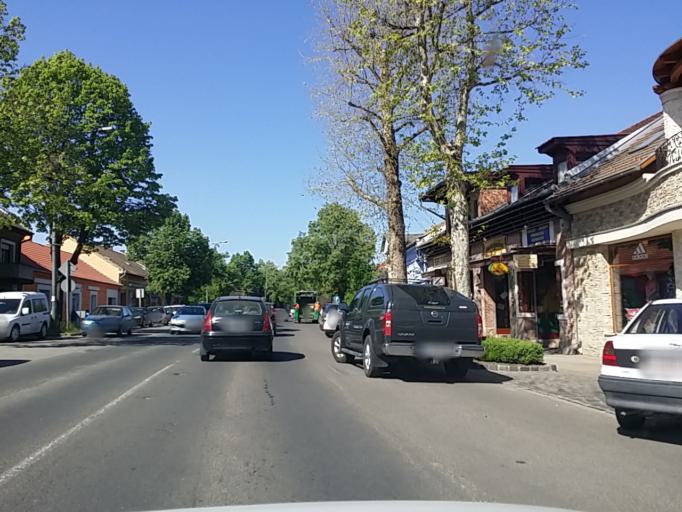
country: HU
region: Pest
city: Aszod
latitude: 47.6512
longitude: 19.4795
